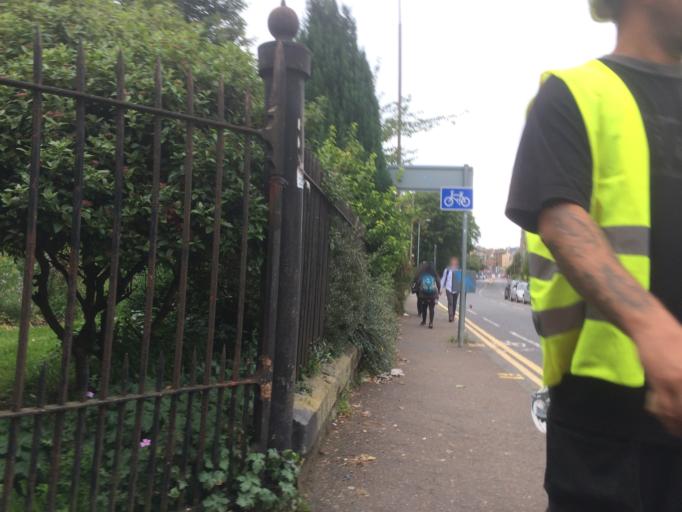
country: GB
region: Scotland
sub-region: Edinburgh
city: Edinburgh
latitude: 55.9299
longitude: -3.1758
